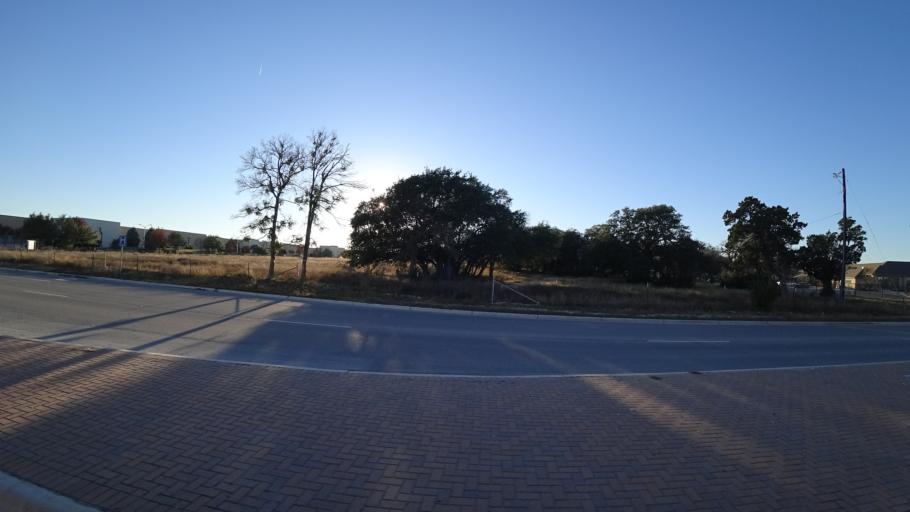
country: US
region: Texas
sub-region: Williamson County
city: Cedar Park
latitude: 30.5311
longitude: -97.8069
